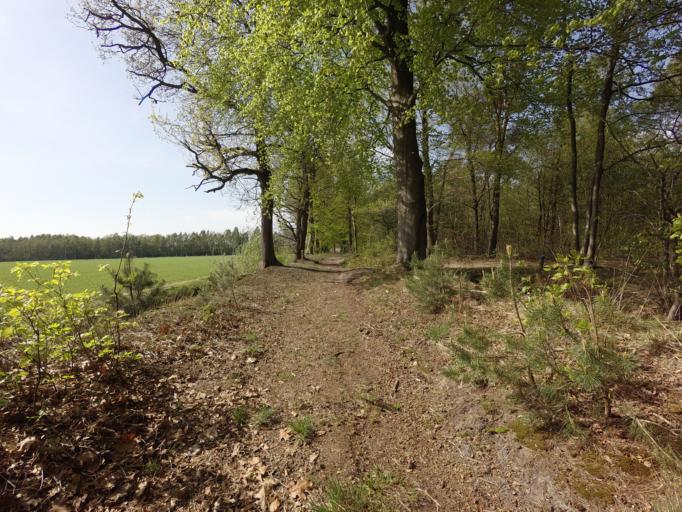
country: NL
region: North Brabant
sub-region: Gemeente Goirle
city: Goirle
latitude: 51.4782
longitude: 5.0014
